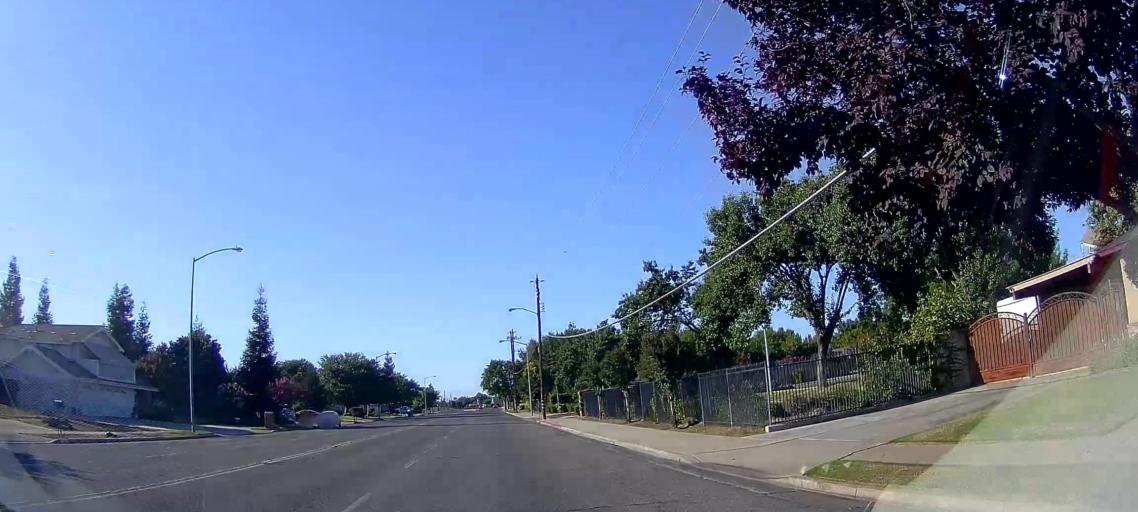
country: US
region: California
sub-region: Fresno County
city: Fresno
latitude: 36.8337
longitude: -119.7993
